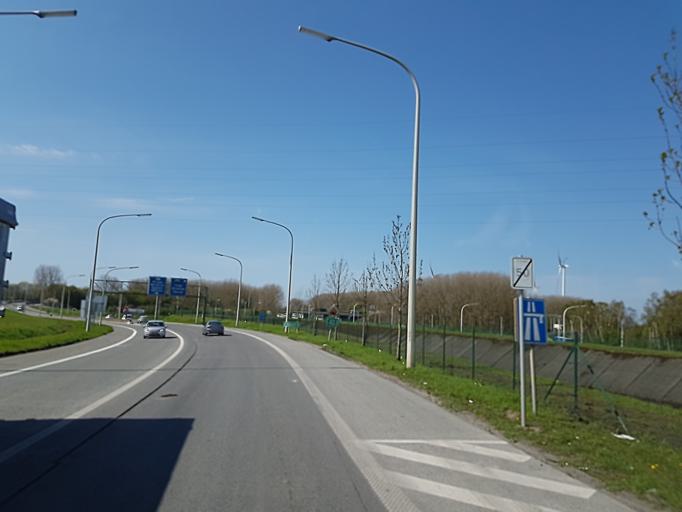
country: BE
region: Wallonia
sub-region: Province du Hainaut
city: Tournai
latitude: 50.6153
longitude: 3.3320
